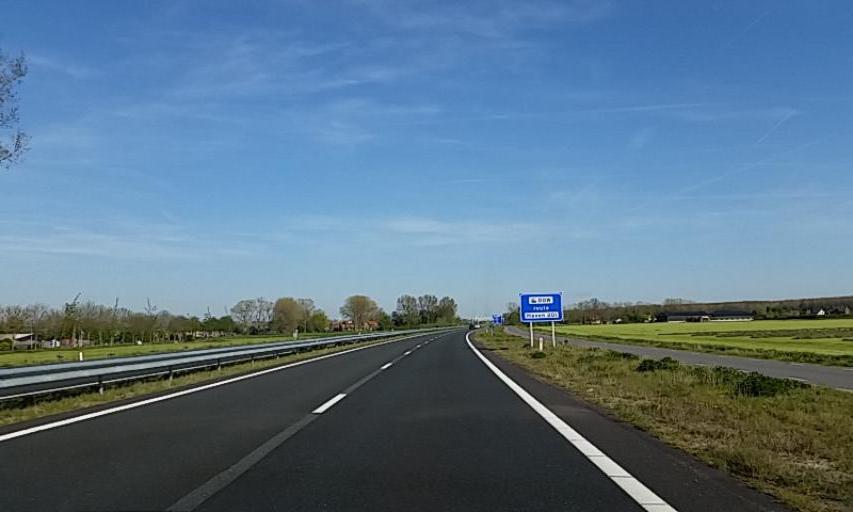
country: NL
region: Zeeland
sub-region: Gemeente Terneuzen
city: Terneuzen
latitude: 51.3066
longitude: 3.7702
